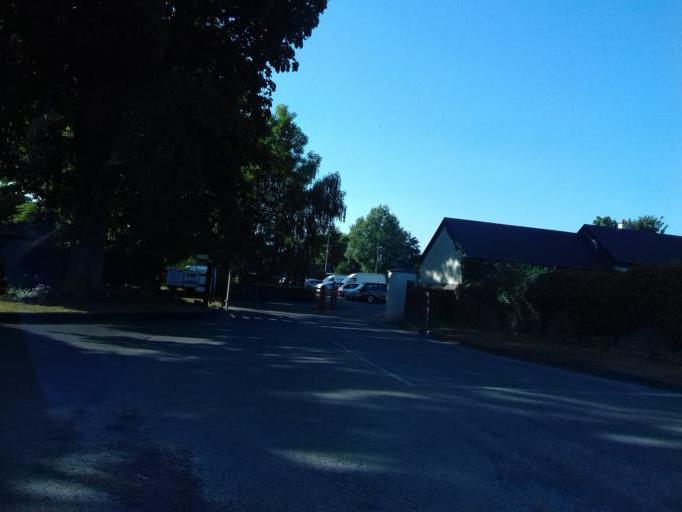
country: IE
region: Leinster
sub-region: Dublin City
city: Finglas
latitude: 53.4591
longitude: -6.3223
